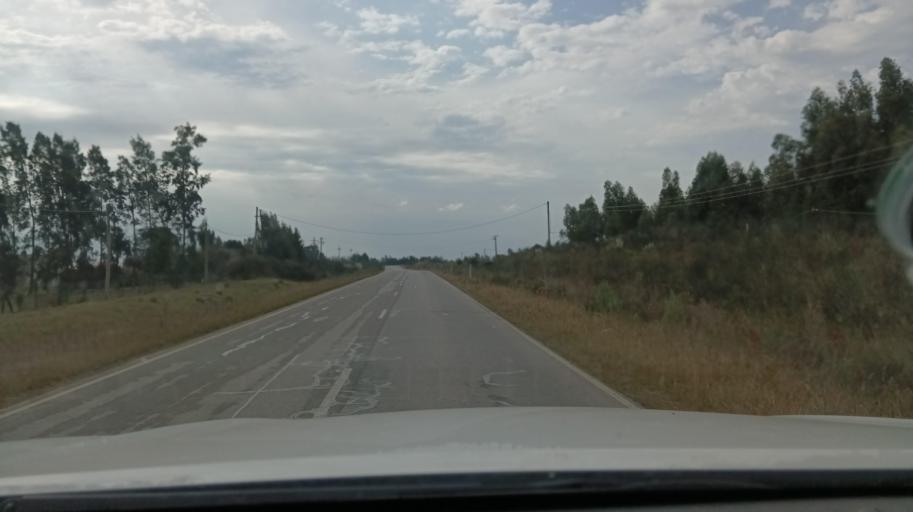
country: UY
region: Canelones
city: Sauce
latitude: -34.6588
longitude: -56.1087
